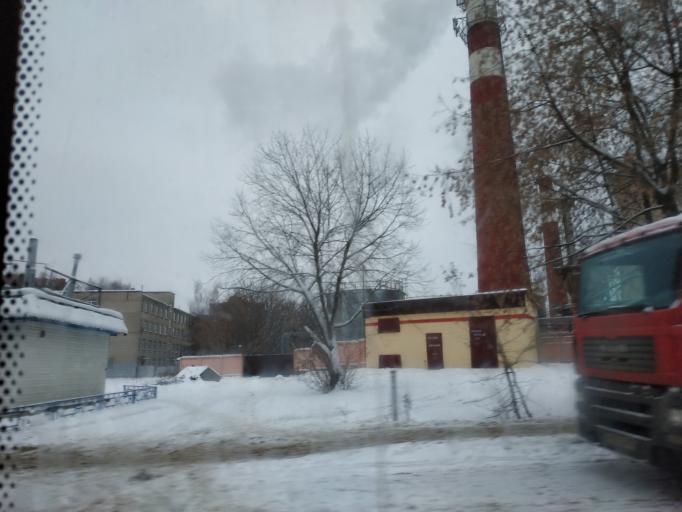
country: RU
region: Moskovskaya
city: Shchelkovo
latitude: 55.9294
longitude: 37.9881
